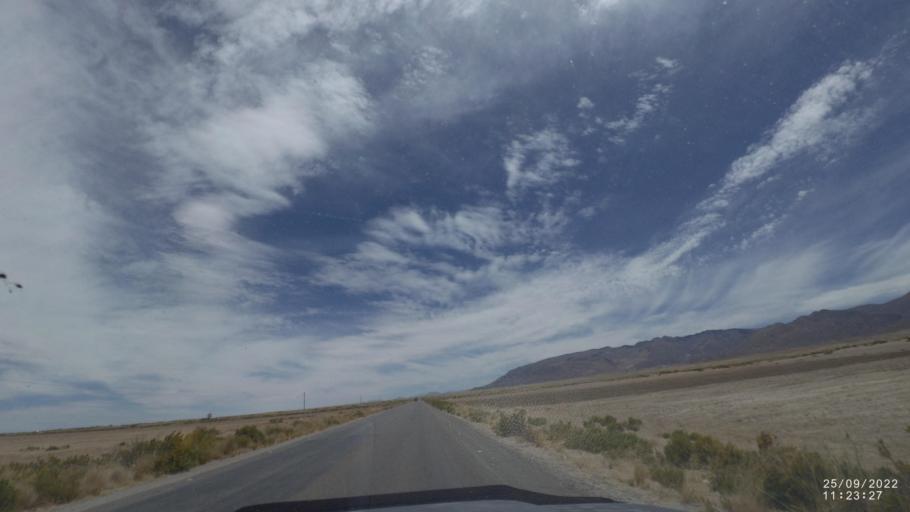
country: BO
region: Oruro
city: Challapata
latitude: -19.1092
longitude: -66.7709
